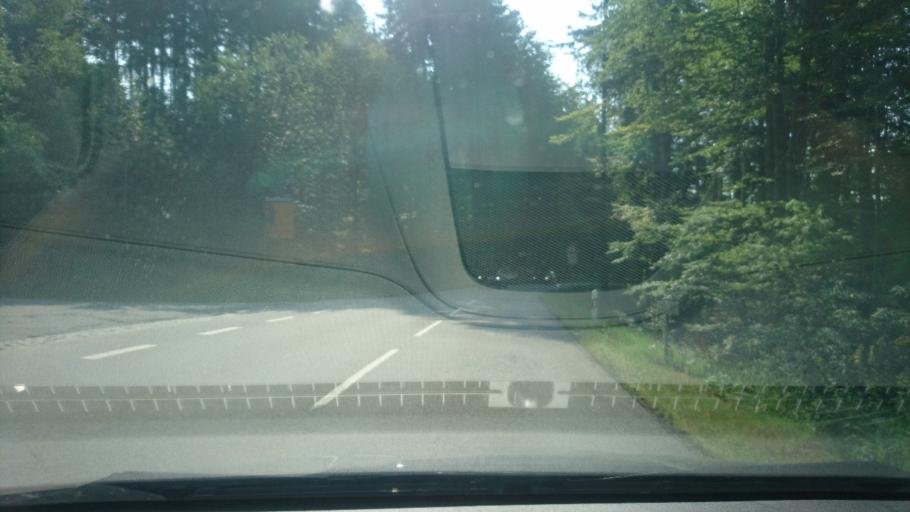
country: DE
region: Bavaria
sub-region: Lower Bavaria
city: Spiegelau
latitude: 48.9083
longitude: 13.3686
